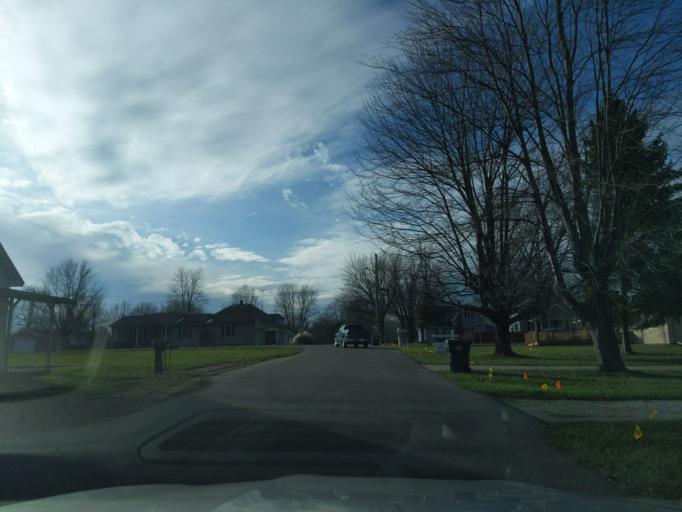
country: US
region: Indiana
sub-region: Decatur County
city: Westport
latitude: 39.1796
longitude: -85.5681
